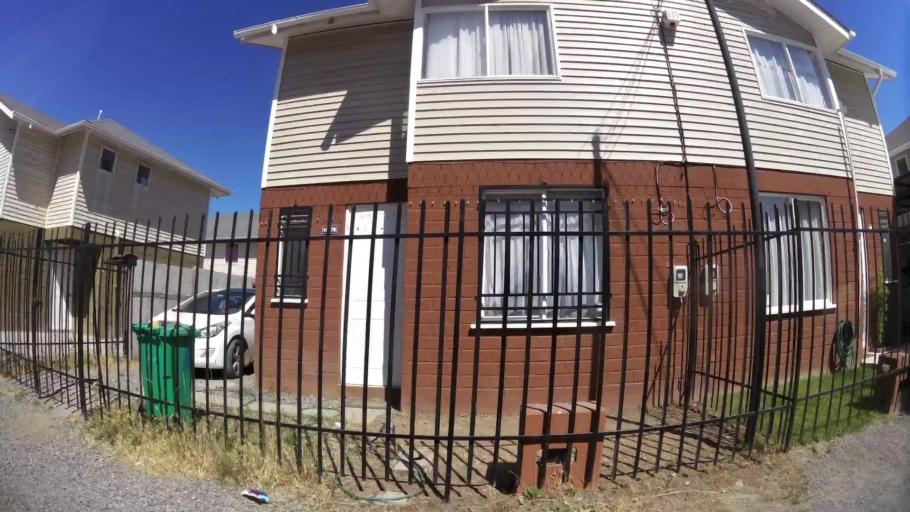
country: CL
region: Santiago Metropolitan
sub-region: Provincia de Maipo
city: San Bernardo
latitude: -33.6122
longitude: -70.6889
